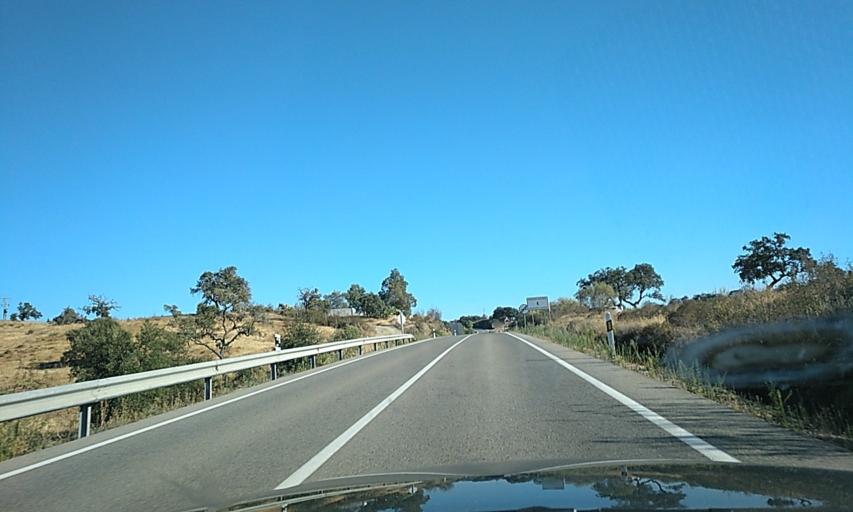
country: ES
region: Andalusia
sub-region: Provincia de Huelva
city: Santa Barbara de Casa
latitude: 37.8005
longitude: -7.1983
